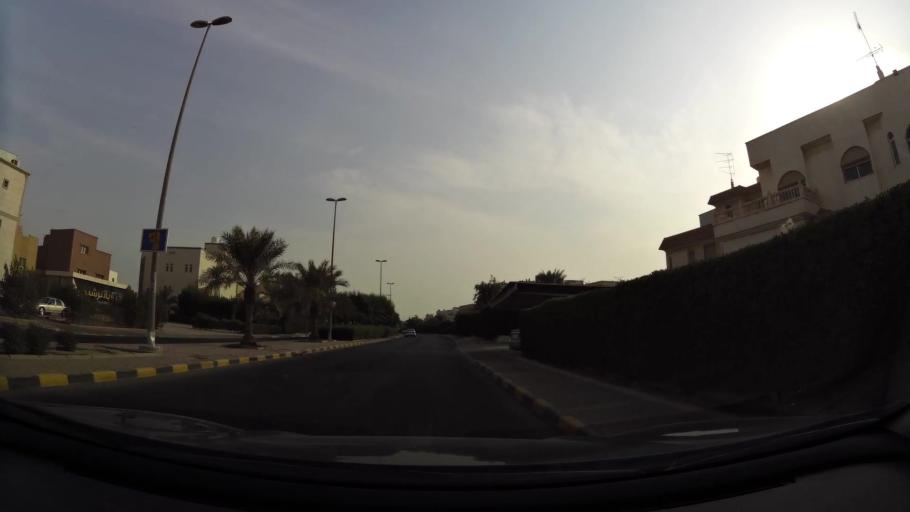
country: KW
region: Mubarak al Kabir
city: Mubarak al Kabir
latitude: 29.1976
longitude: 48.0685
